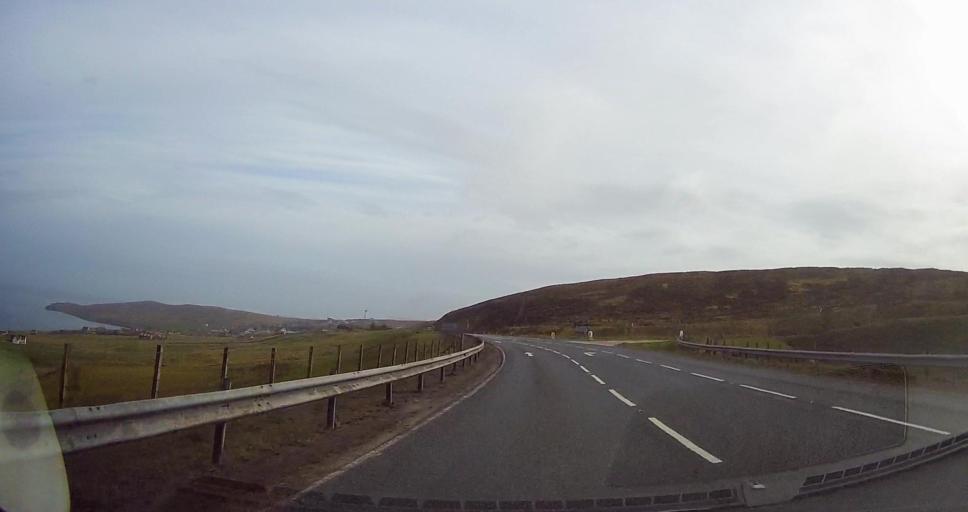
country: GB
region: Scotland
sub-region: Shetland Islands
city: Lerwick
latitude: 60.1379
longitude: -1.2126
